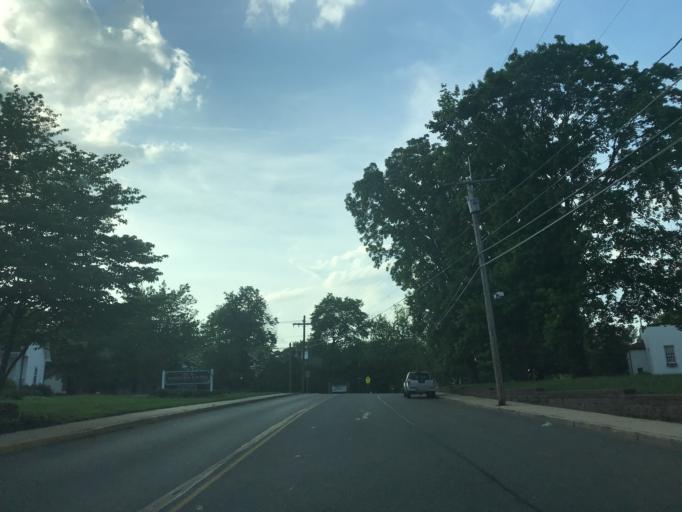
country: US
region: Maryland
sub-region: Harford County
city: Bel Air
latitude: 39.5404
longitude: -76.3492
